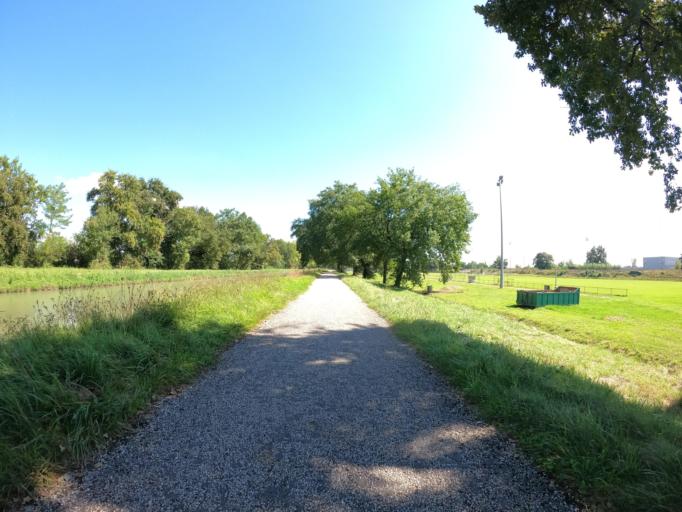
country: FR
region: Midi-Pyrenees
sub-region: Departement du Tarn-et-Garonne
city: Valence
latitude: 44.1163
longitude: 0.8602
